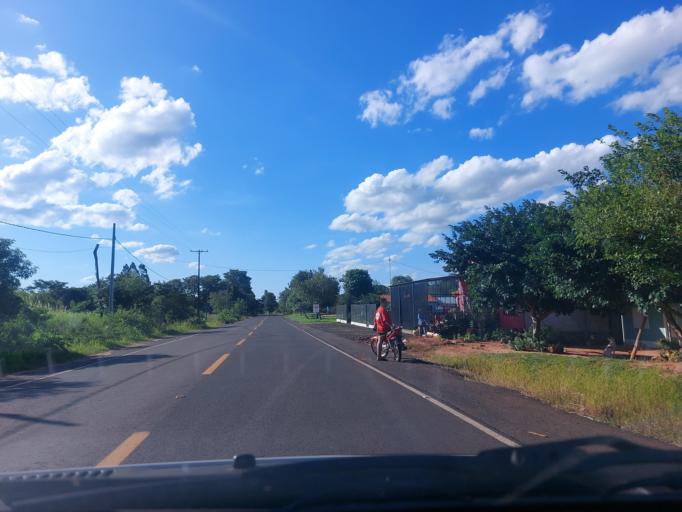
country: PY
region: San Pedro
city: Guayaybi
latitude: -24.5713
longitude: -56.5195
